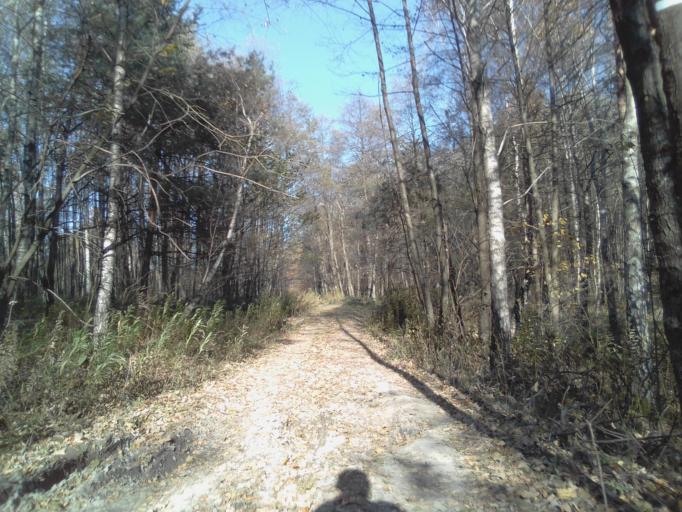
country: PL
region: Subcarpathian Voivodeship
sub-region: Powiat strzyzowski
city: Wysoka Strzyzowska
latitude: 49.7993
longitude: 21.7274
